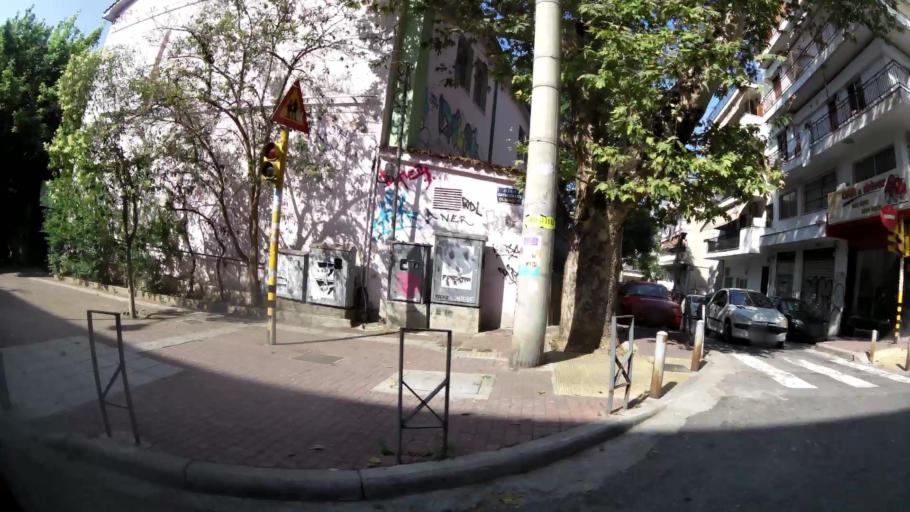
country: GR
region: Central Macedonia
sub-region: Nomos Thessalonikis
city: Agios Pavlos
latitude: 40.6391
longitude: 22.9522
